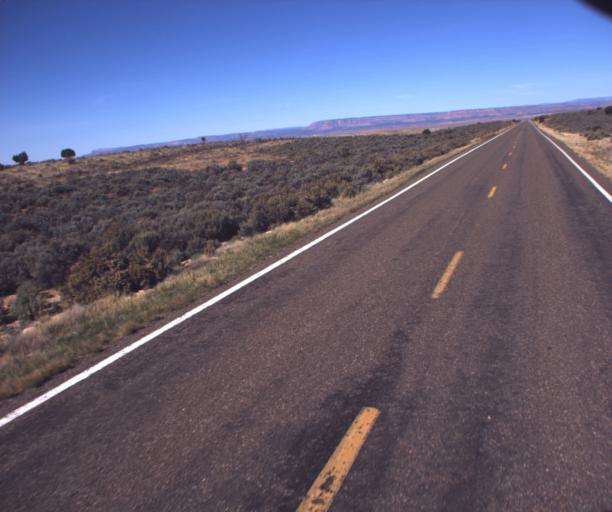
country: US
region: Arizona
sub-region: Coconino County
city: Fredonia
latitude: 36.8627
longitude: -112.3136
